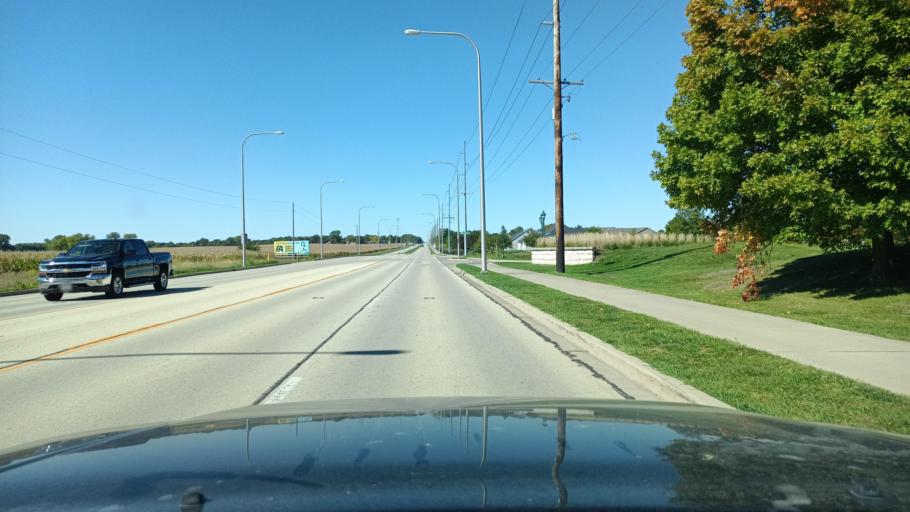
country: US
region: Illinois
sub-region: Champaign County
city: Urbana
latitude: 40.0841
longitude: -88.1677
